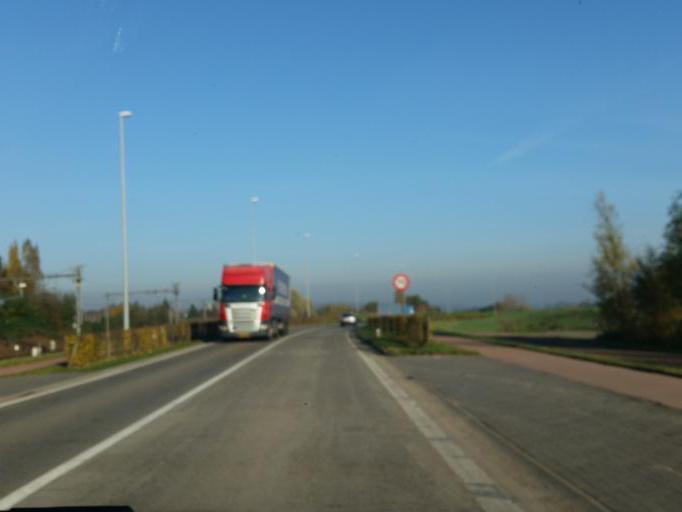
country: BE
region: Flanders
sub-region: Provincie Vlaams-Brabant
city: Asse
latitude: 50.9092
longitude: 4.2077
